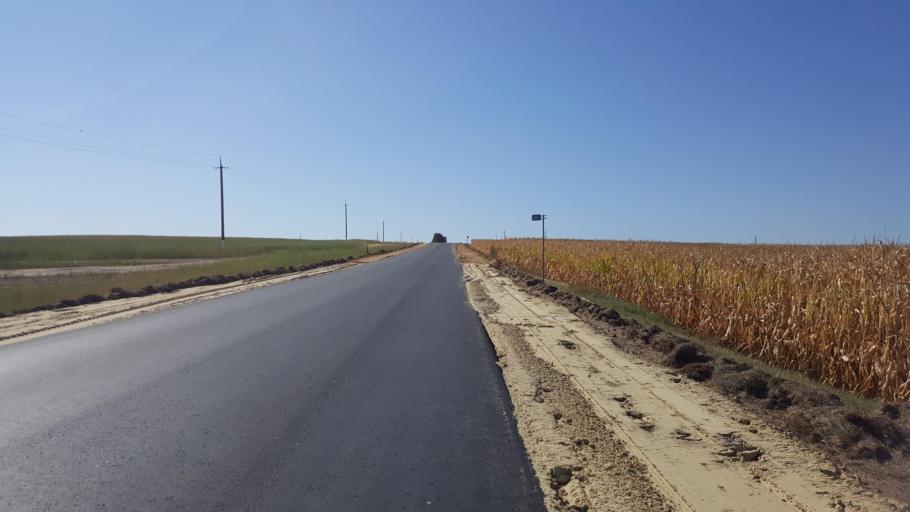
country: BY
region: Brest
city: Charnawchytsy
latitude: 52.2907
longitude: 23.6053
